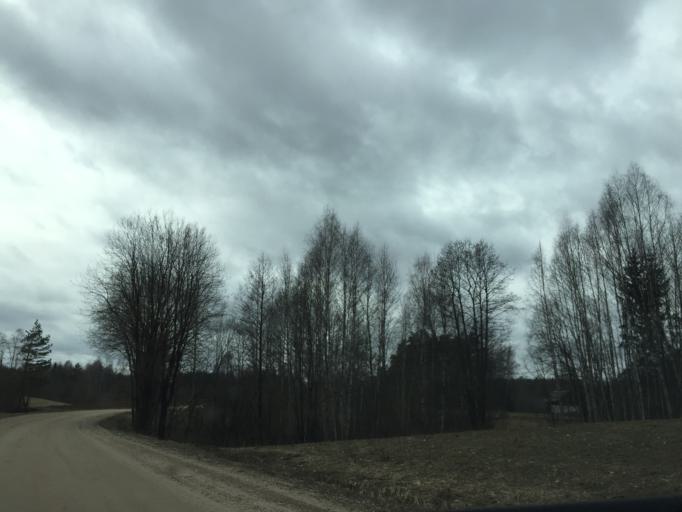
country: LV
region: Kraslavas Rajons
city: Kraslava
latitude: 55.9640
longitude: 27.0627
